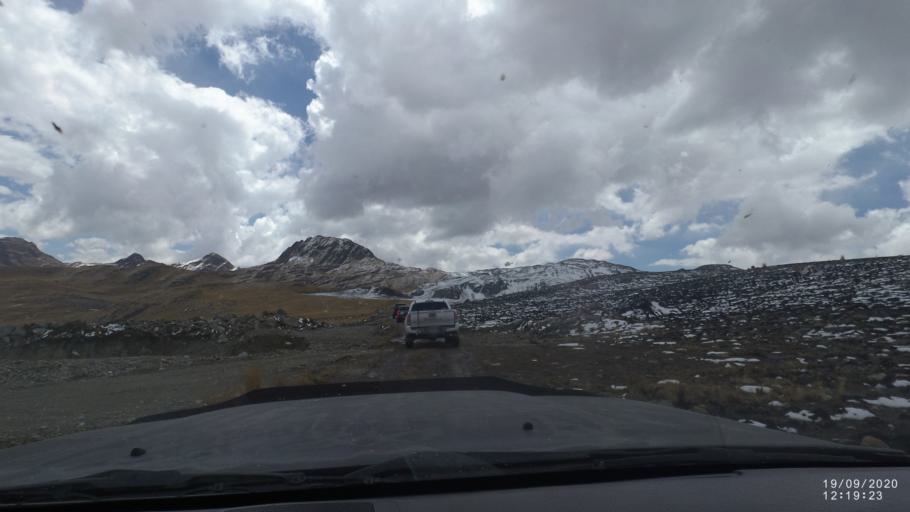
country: BO
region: Cochabamba
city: Cochabamba
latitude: -17.2996
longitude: -66.1085
